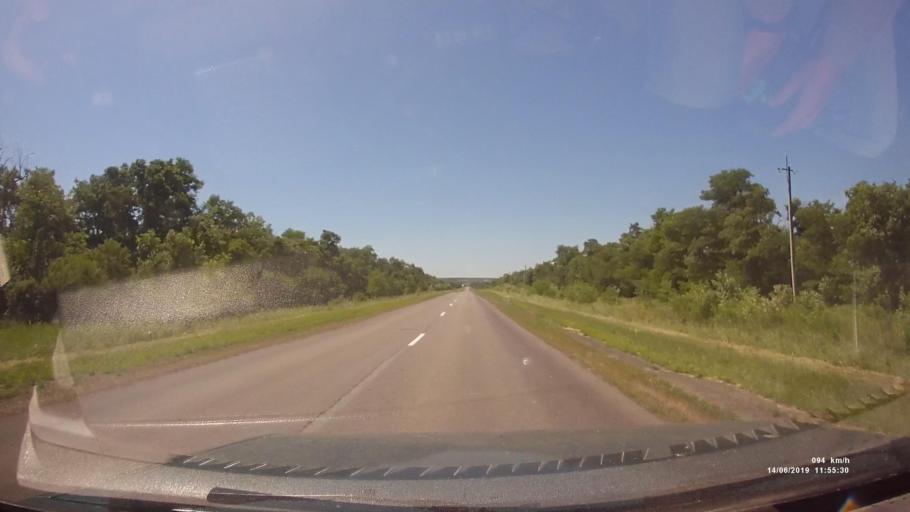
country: RU
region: Rostov
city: Kazanskaya
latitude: 49.8100
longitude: 41.1760
